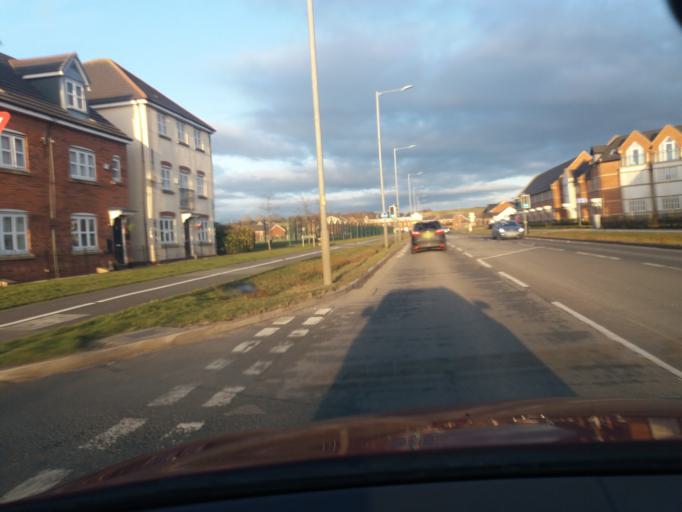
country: GB
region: England
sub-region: Lancashire
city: Euxton
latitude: 53.6769
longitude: -2.6599
